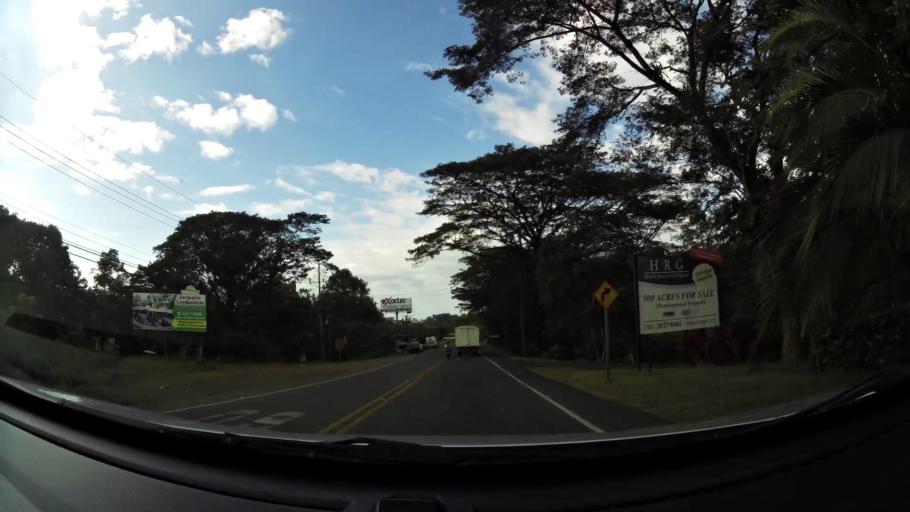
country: CR
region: Puntarenas
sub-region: Canton de Garabito
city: Jaco
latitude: 9.7083
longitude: -84.6355
